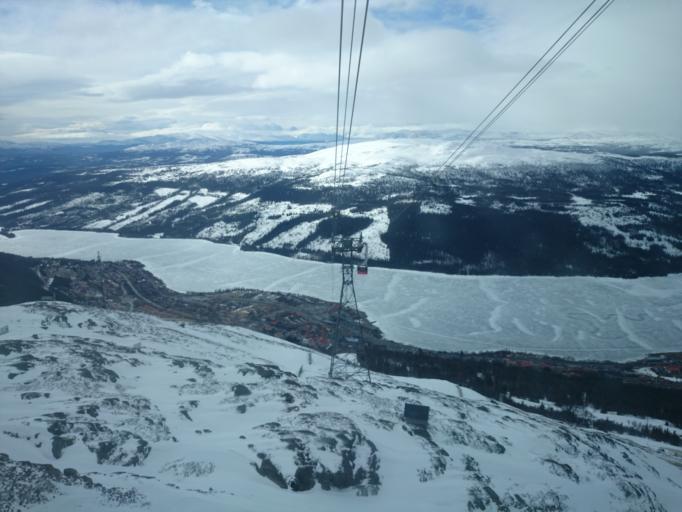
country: SE
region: Jaemtland
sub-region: Are Kommun
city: Are
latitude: 63.4151
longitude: 13.0781
